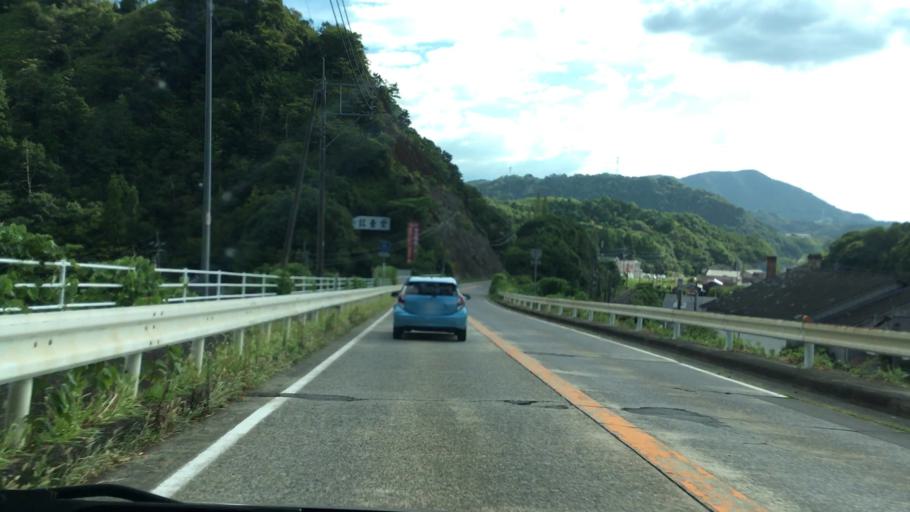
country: JP
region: Saga Prefecture
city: Imaricho-ko
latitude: 33.1847
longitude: 129.8938
